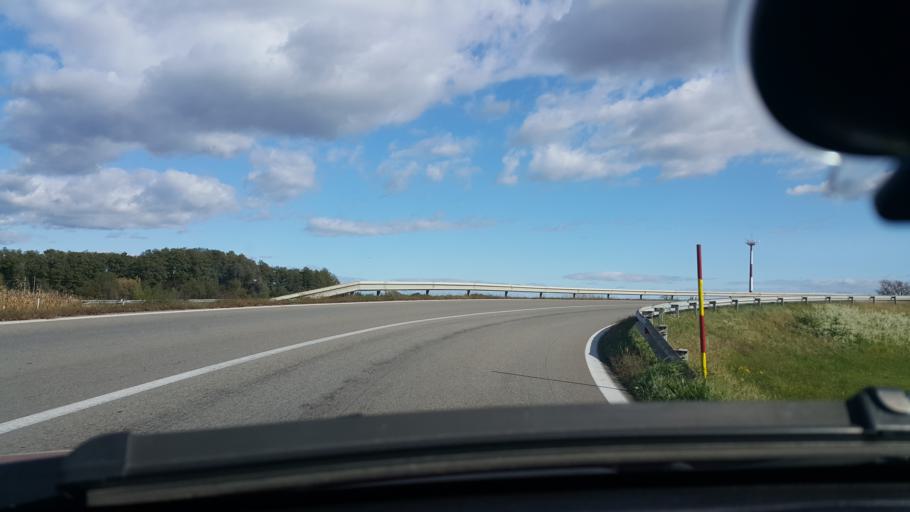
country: SI
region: Race-Fram
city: Fram
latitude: 46.4505
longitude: 15.6487
